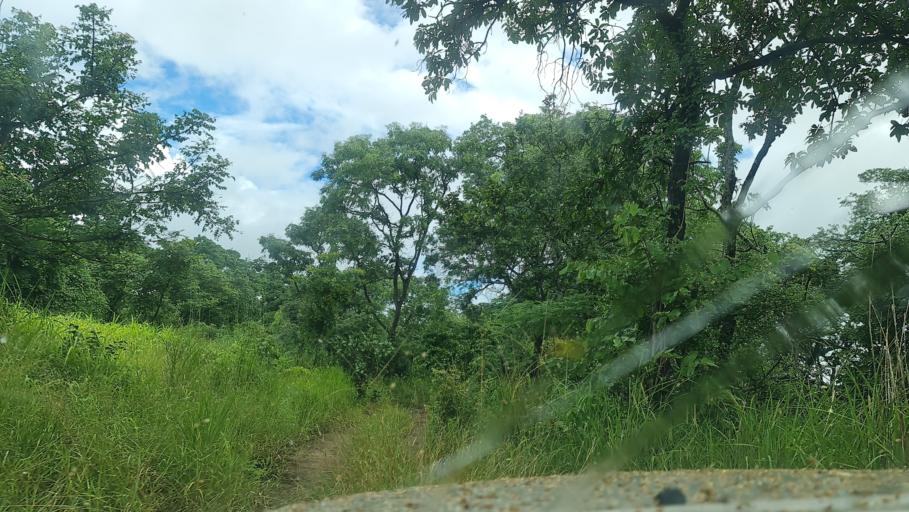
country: MW
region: Southern Region
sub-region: Nsanje District
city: Nsanje
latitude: -17.4478
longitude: 35.8413
